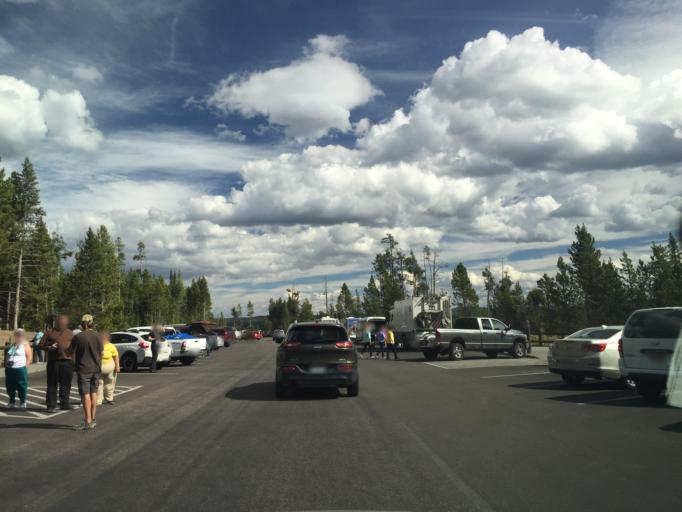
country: US
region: Montana
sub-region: Gallatin County
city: West Yellowstone
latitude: 44.7197
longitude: -110.4979
